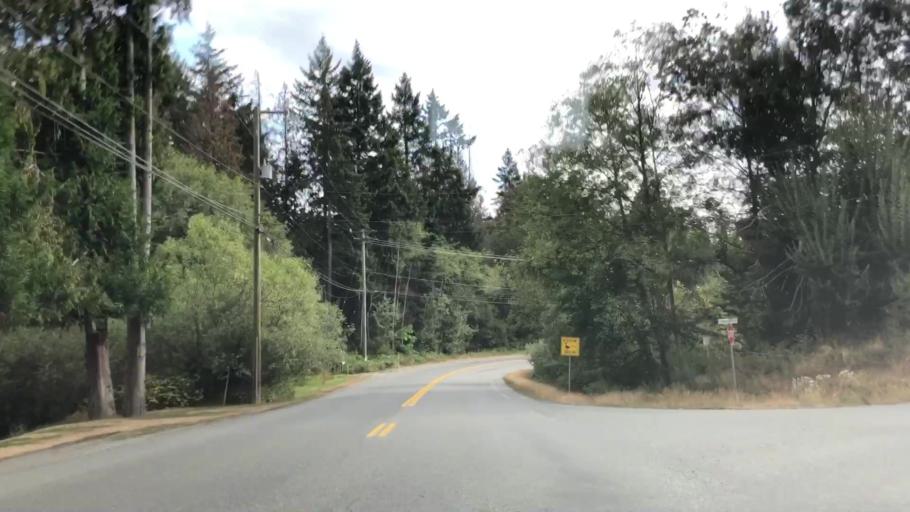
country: CA
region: British Columbia
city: North Saanich
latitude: 48.6875
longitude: -123.5698
